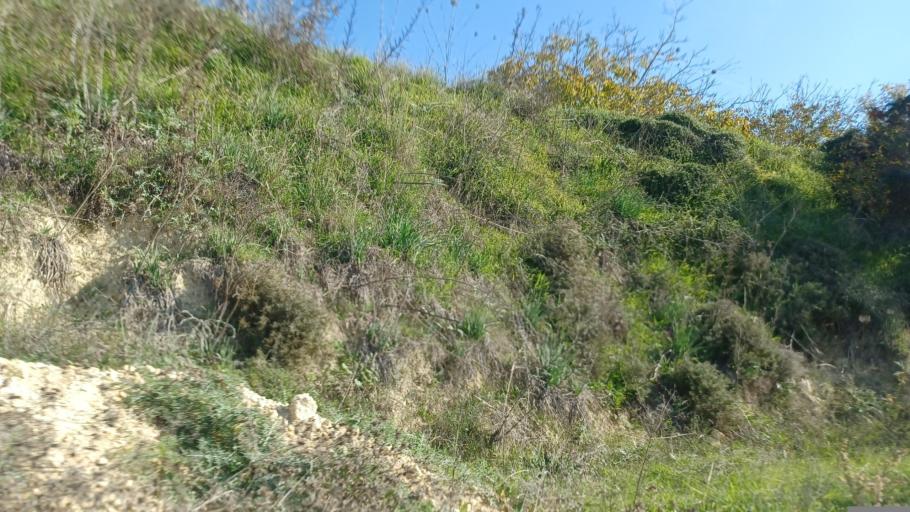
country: CY
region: Pafos
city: Mesogi
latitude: 34.8363
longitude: 32.5232
